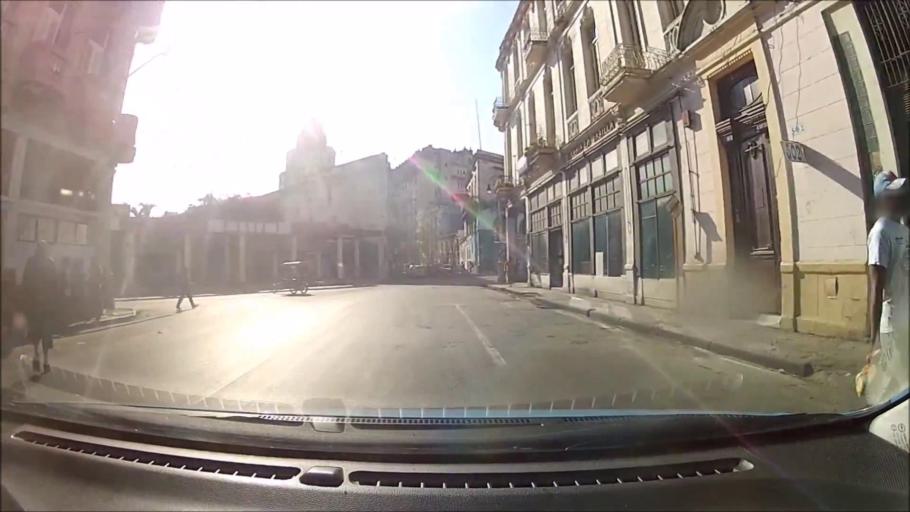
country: CU
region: La Habana
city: Centro Habana
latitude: 23.1345
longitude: -82.3633
